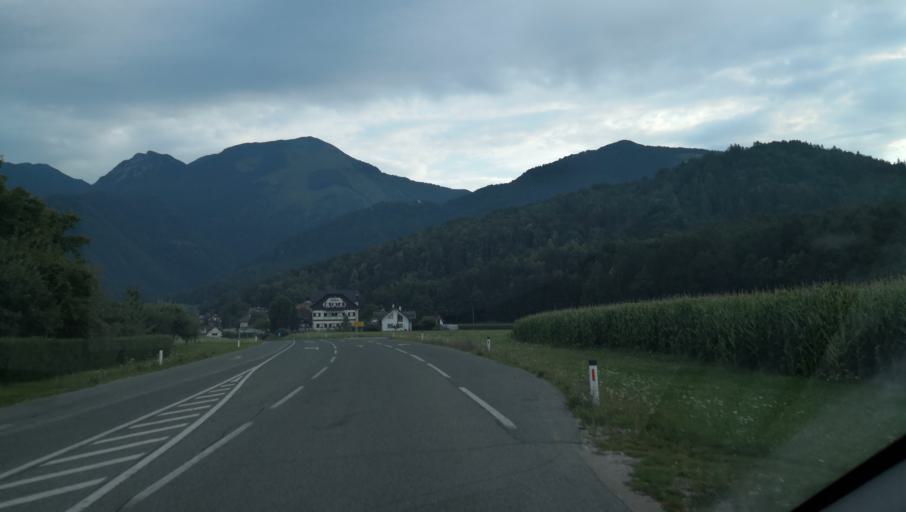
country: SI
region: Preddvor
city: Preddvor
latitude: 46.2914
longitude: 14.4296
